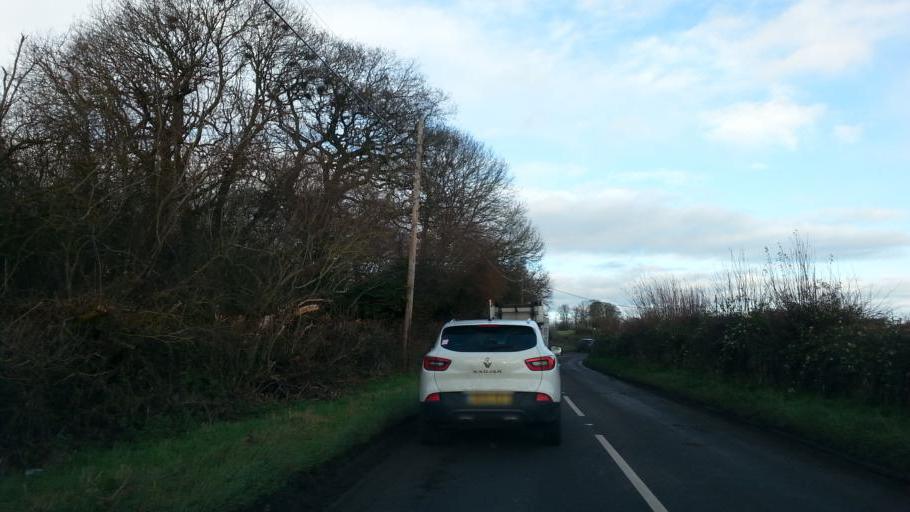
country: GB
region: England
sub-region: Oxfordshire
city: Faringdon
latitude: 51.6230
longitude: -1.5854
